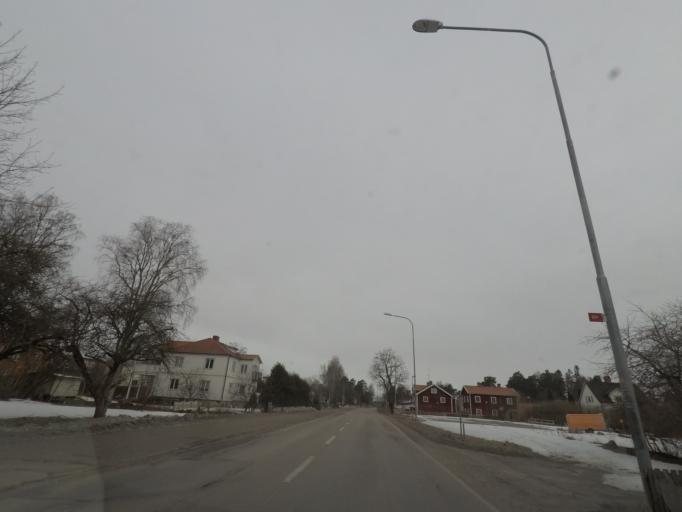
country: SE
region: Vaestmanland
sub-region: Vasteras
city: Skultuna
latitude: 59.7168
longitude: 16.4300
